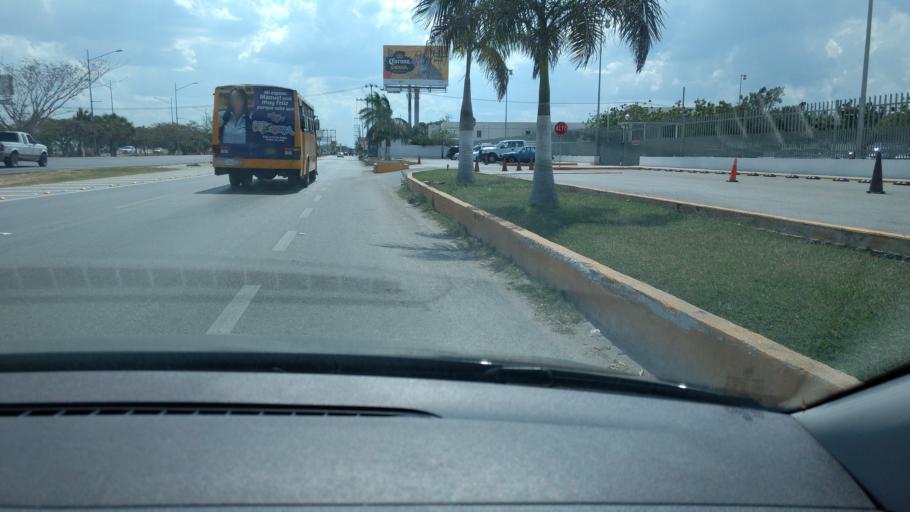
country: MX
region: Yucatan
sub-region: Kanasin
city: Kanasin
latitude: 20.9782
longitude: -89.5647
